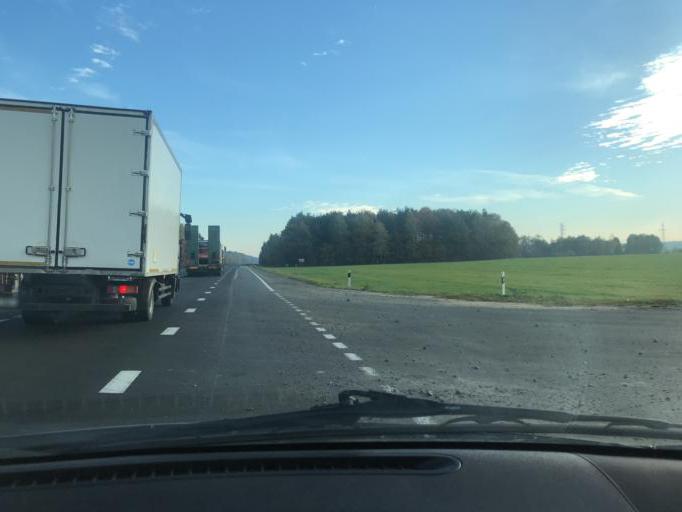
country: BY
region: Brest
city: Drahichyn
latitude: 52.2151
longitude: 25.0957
